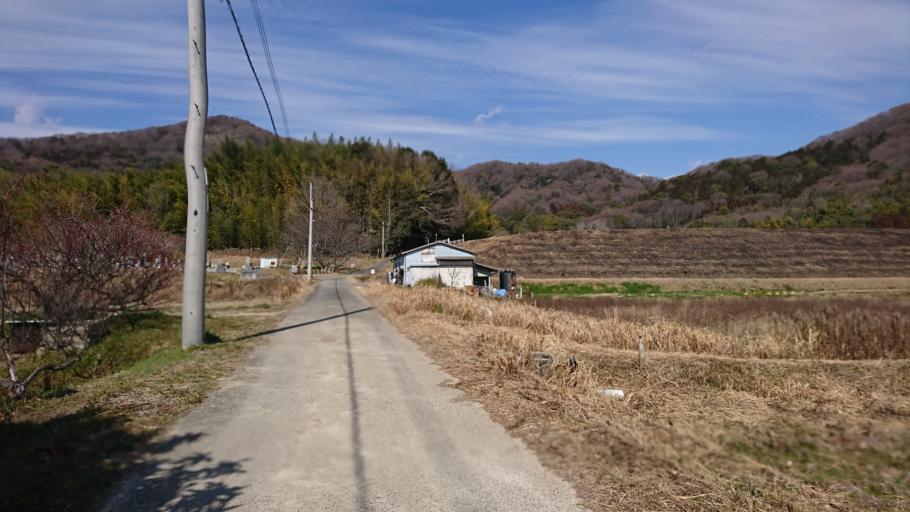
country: JP
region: Hyogo
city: Kakogawacho-honmachi
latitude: 34.8265
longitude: 134.8086
